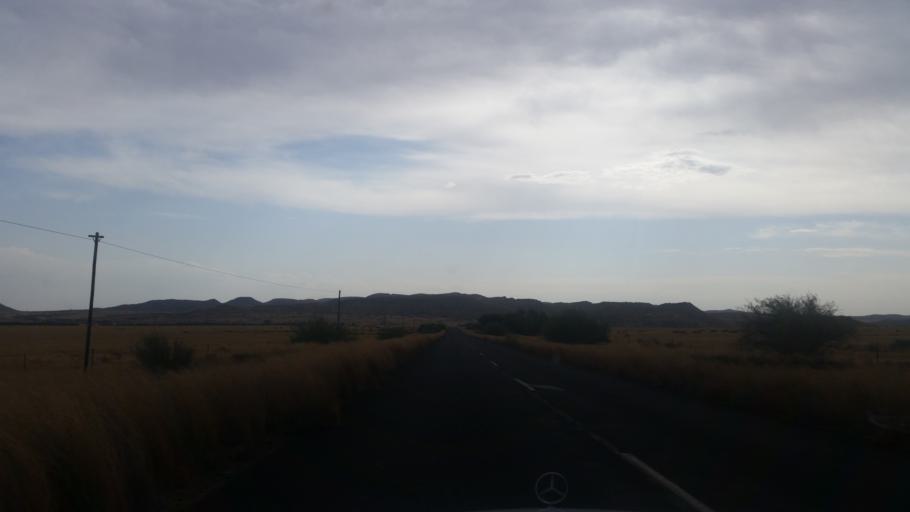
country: ZA
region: Orange Free State
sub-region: Xhariep District Municipality
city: Trompsburg
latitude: -30.4248
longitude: 26.1291
